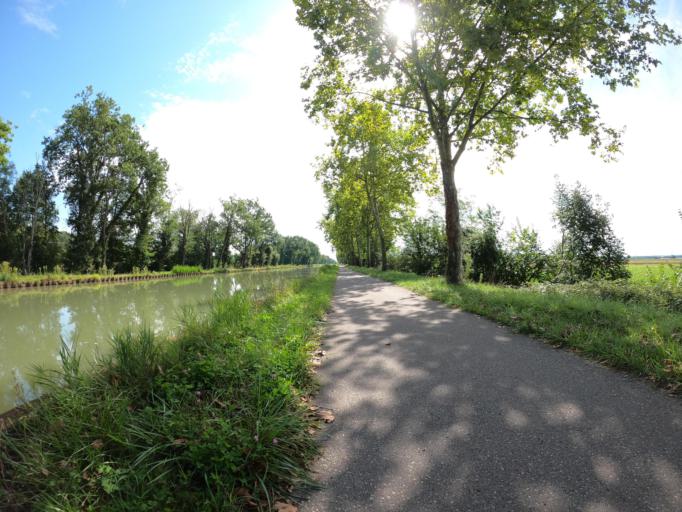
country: FR
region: Midi-Pyrenees
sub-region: Departement du Tarn-et-Garonne
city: Grisolles
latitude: 43.8555
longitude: 1.2824
